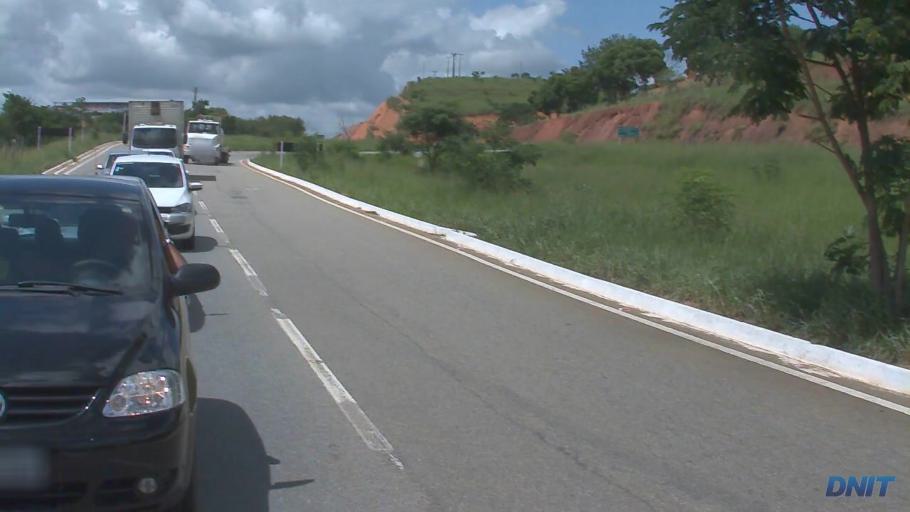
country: BR
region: Minas Gerais
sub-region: Governador Valadares
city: Governador Valadares
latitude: -18.9091
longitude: -42.0061
